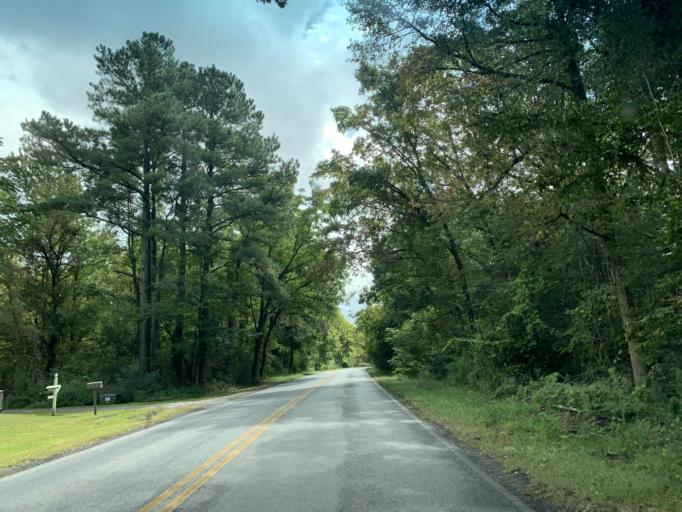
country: US
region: Maryland
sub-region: Caroline County
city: Denton
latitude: 38.9018
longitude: -75.8383
